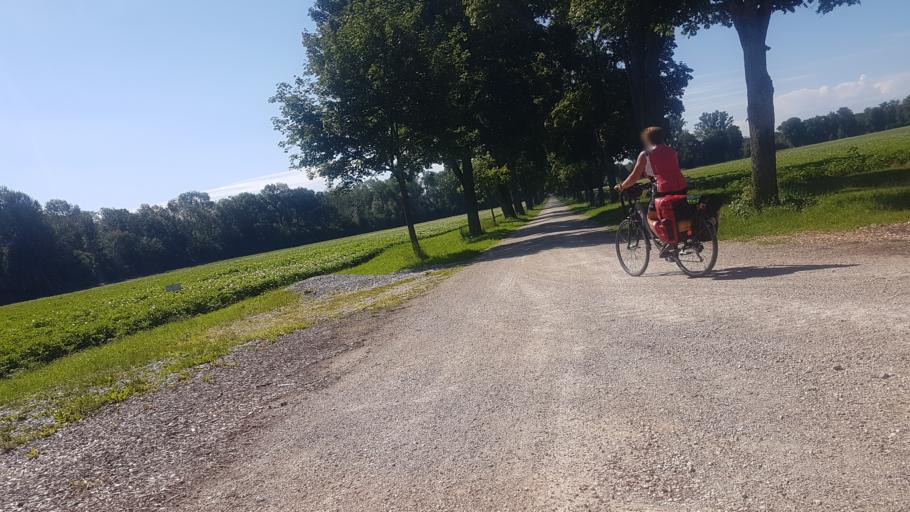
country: DE
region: Bavaria
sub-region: Upper Bavaria
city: Bergheim
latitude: 48.7370
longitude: 11.2651
